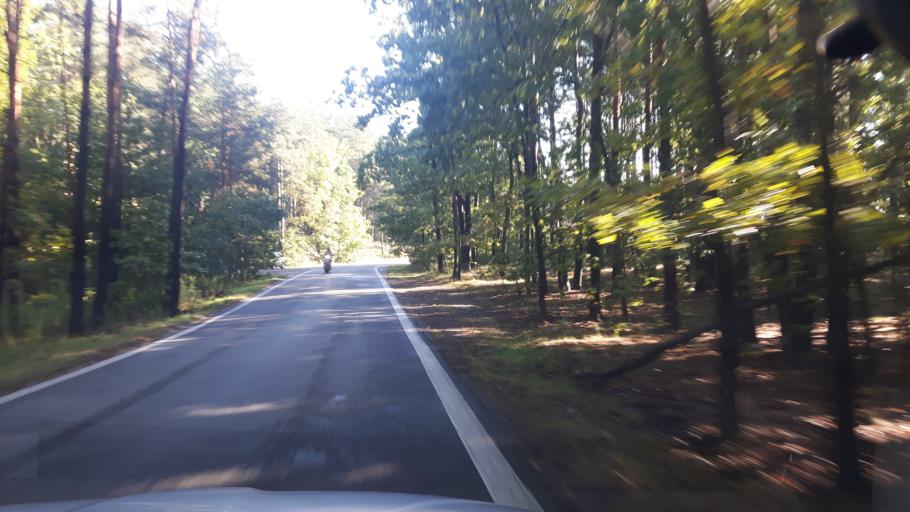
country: PL
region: Masovian Voivodeship
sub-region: Warszawa
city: Bialoleka
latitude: 52.3490
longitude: 21.0085
